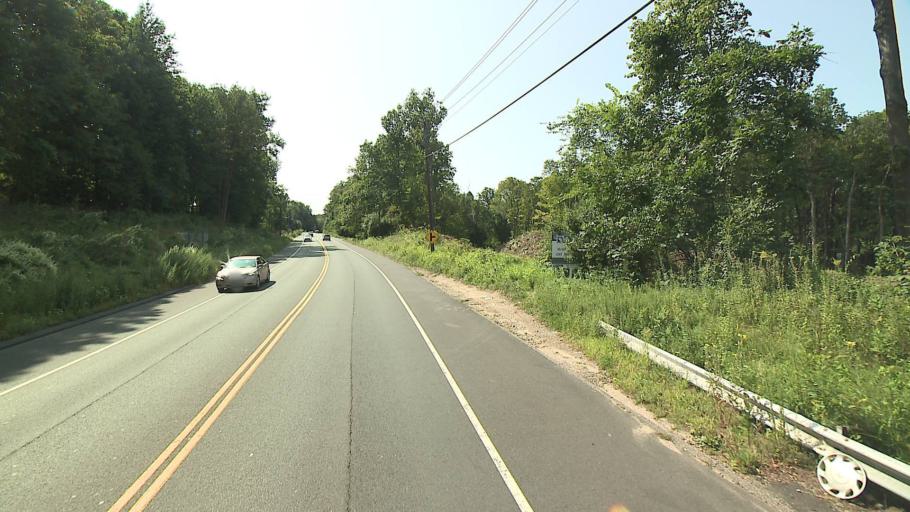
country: US
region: Connecticut
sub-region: Fairfield County
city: Newtown
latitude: 41.4231
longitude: -73.3557
